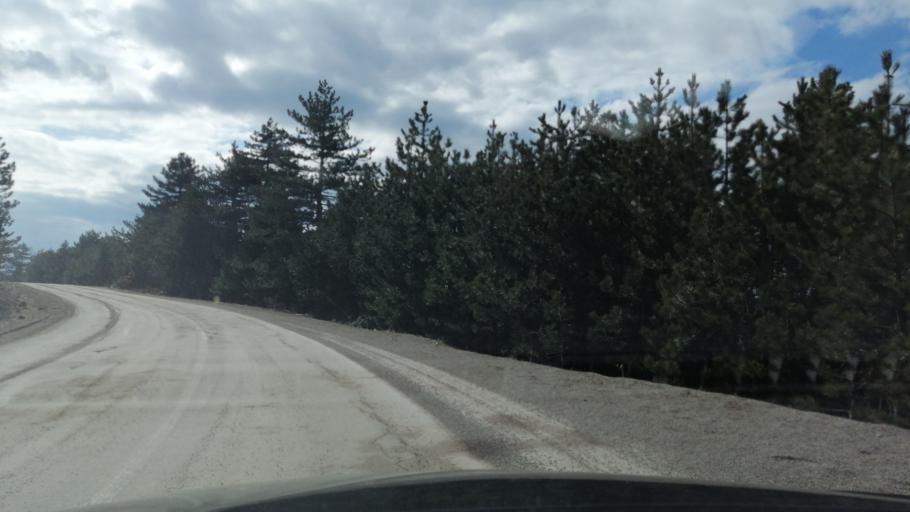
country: RS
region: Central Serbia
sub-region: Zlatiborski Okrug
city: Bajina Basta
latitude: 43.8835
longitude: 19.5465
